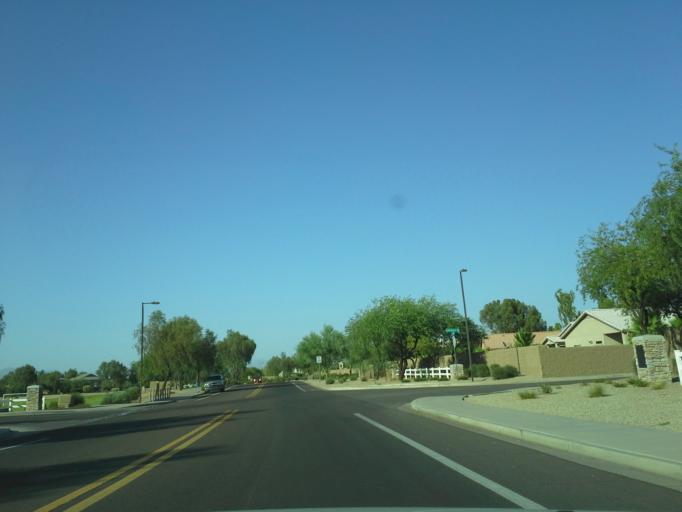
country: US
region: Arizona
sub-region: Pinal County
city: San Tan Valley
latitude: 33.1412
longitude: -111.5573
